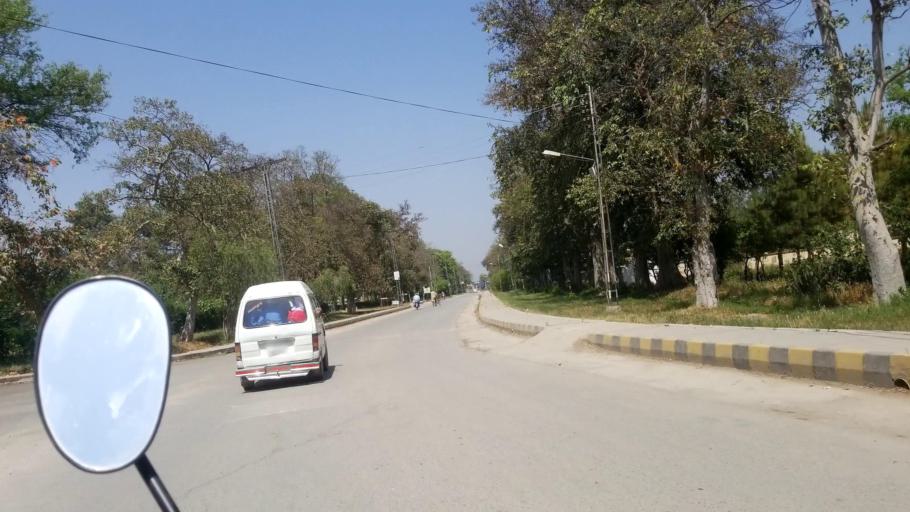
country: PK
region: Khyber Pakhtunkhwa
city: Peshawar
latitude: 34.0152
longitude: 71.4836
